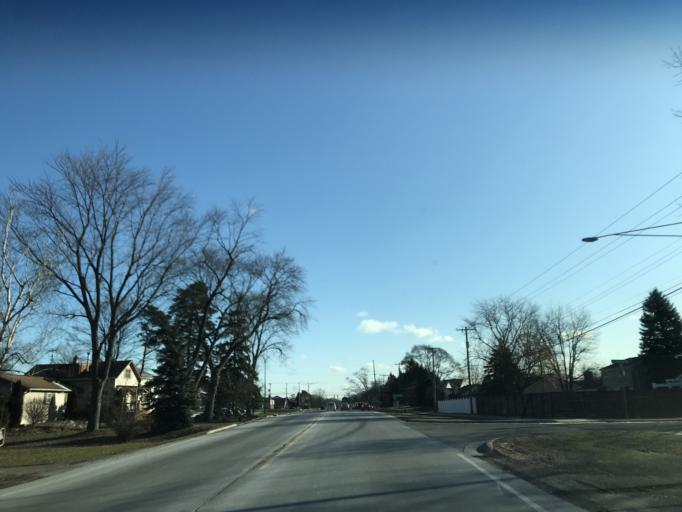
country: US
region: Michigan
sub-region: Oakland County
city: Troy
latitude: 42.5772
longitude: -83.1518
